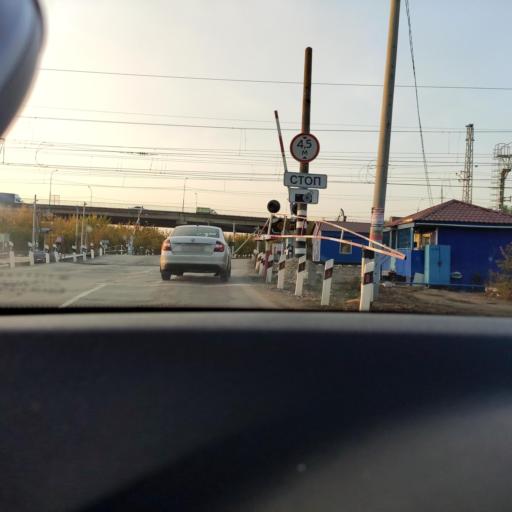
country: RU
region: Samara
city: Smyshlyayevka
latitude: 53.2530
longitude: 50.3682
